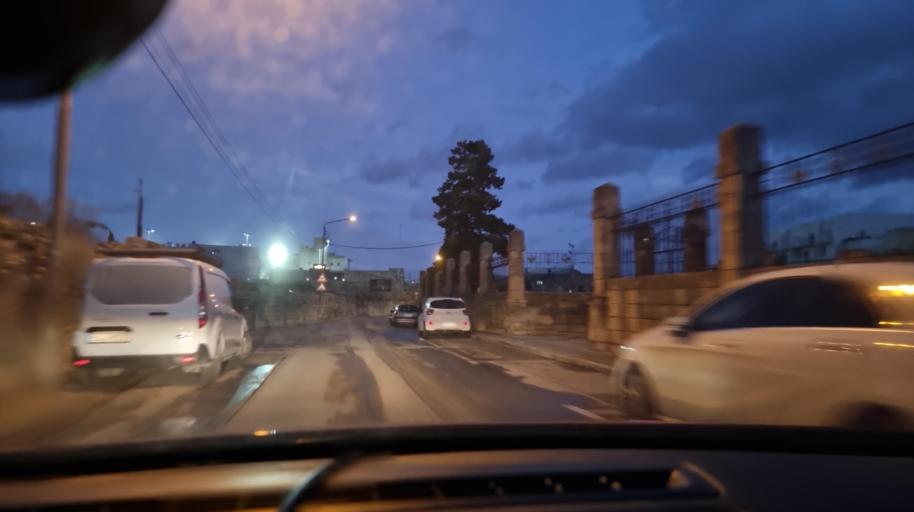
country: MT
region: Qormi
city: Qormi
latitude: 35.8826
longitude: 14.4746
